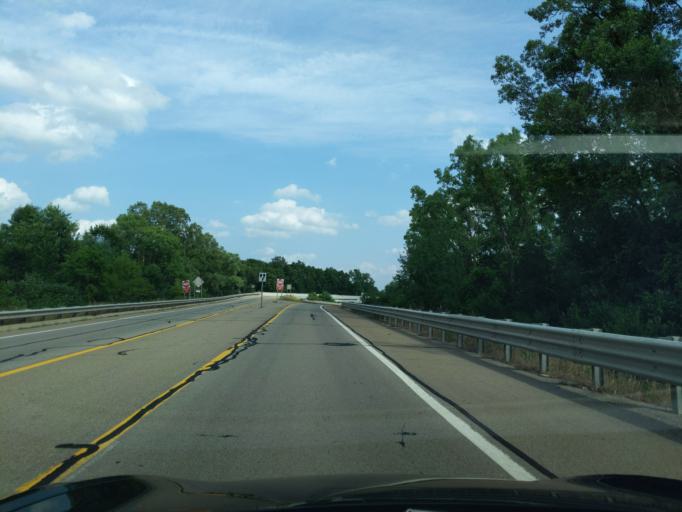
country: US
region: Michigan
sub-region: Jackson County
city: Jackson
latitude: 42.2981
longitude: -84.4352
